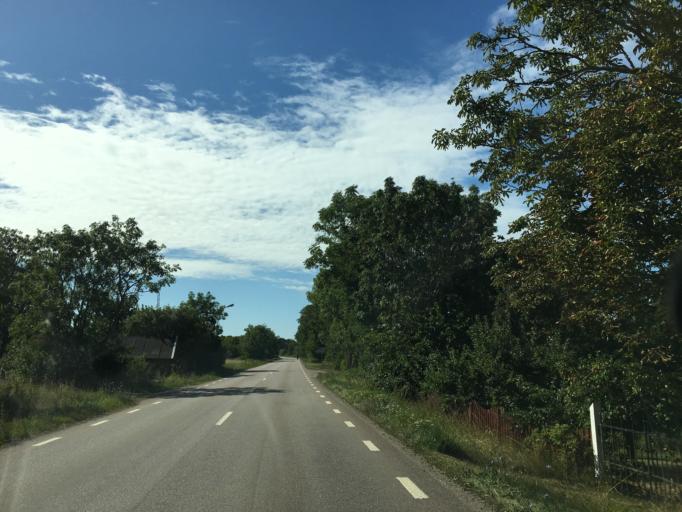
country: SE
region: Kalmar
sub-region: Morbylanga Kommun
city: Moerbylanga
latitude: 56.5206
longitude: 16.4400
